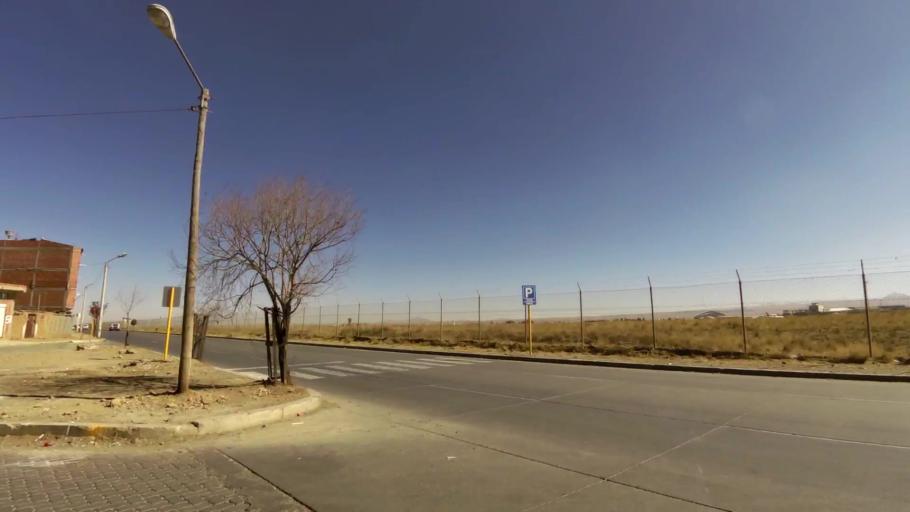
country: BO
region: La Paz
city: La Paz
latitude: -16.5162
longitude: -68.1763
